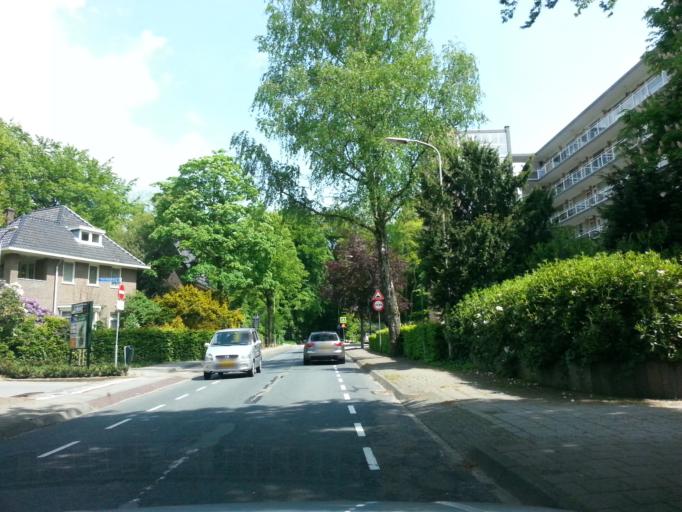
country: NL
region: Gelderland
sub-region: Gemeente Renkum
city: Oosterbeek
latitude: 51.9873
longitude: 5.8572
